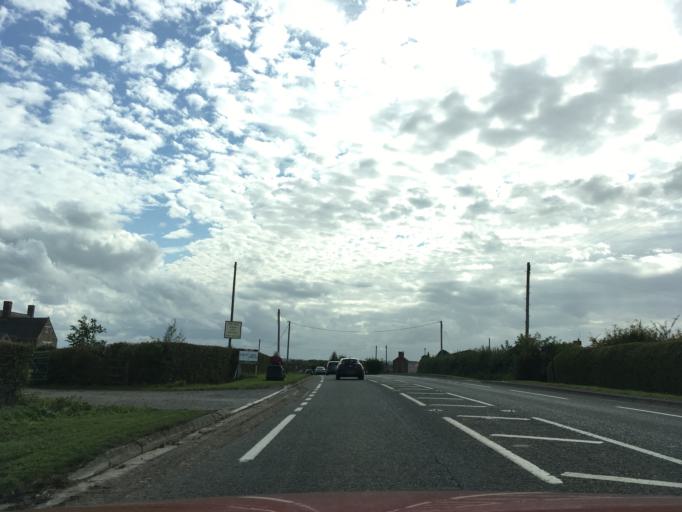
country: GB
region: England
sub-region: Gloucestershire
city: Berkeley
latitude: 51.6850
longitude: -2.4322
